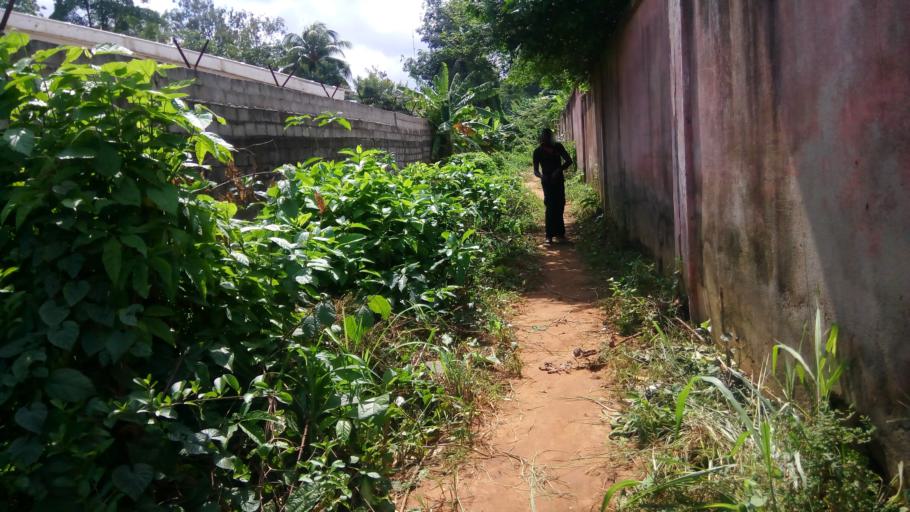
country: CI
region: Lagunes
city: Abidjan
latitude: 5.3405
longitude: -3.9950
